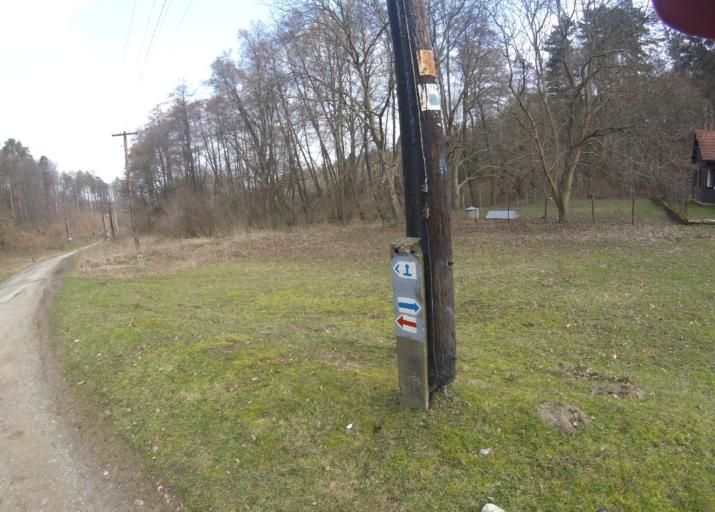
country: HU
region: Heves
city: Belapatfalva
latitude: 48.0384
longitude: 20.3529
